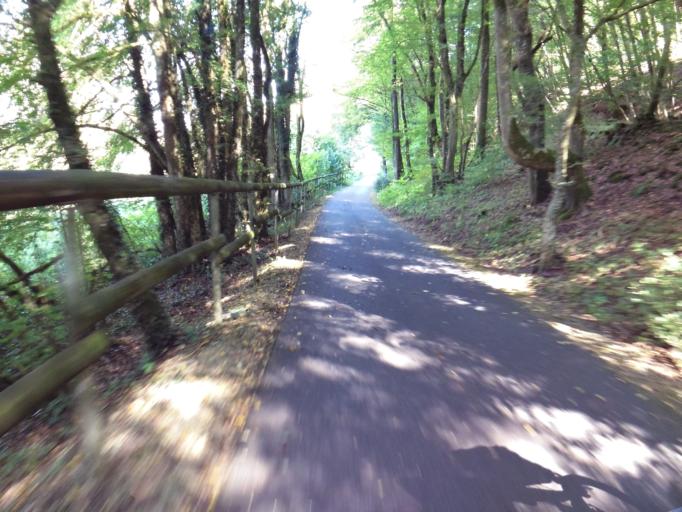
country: LU
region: Grevenmacher
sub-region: Canton d'Echternach
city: Rosport
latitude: 49.7777
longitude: 6.5131
